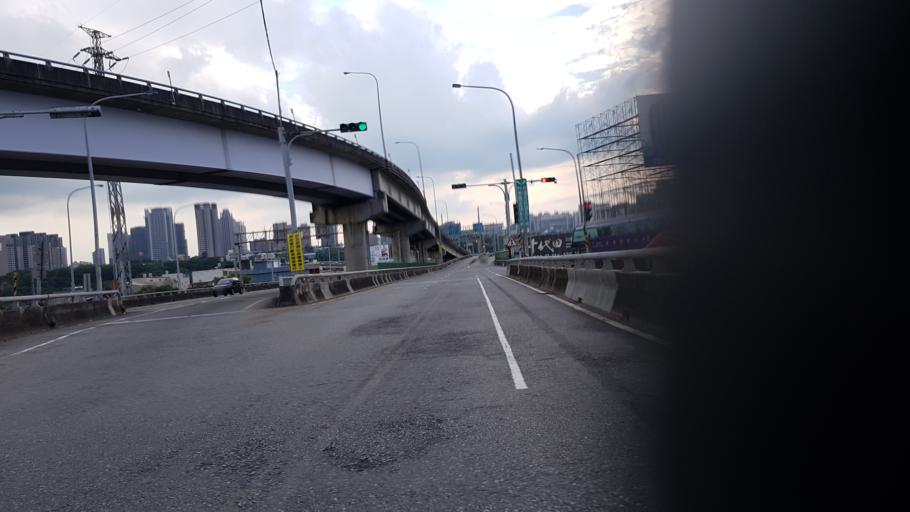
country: TW
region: Taiwan
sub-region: Hsinchu
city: Zhubei
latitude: 24.8051
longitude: 121.0166
